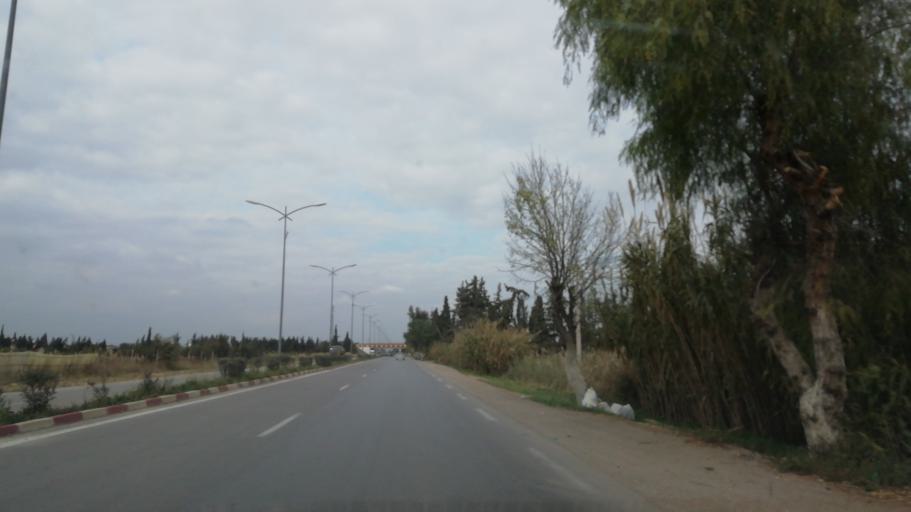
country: DZ
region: Mascara
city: Mascara
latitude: 35.6182
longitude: 0.0623
